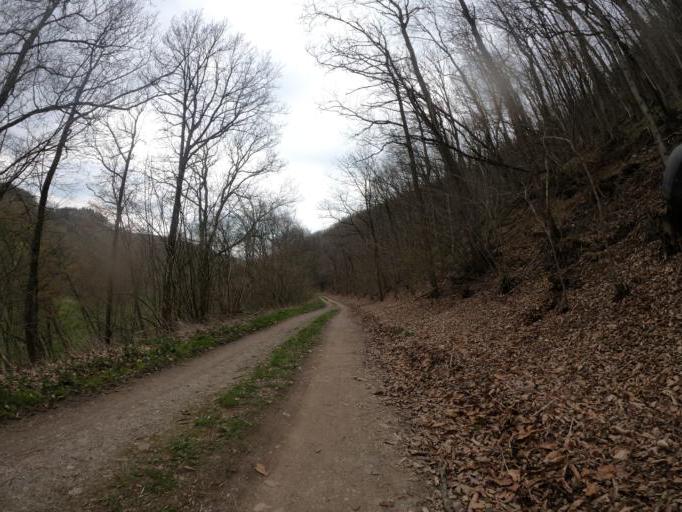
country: DE
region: North Rhine-Westphalia
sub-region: Regierungsbezirk Koln
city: Nideggen
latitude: 50.6813
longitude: 6.4247
